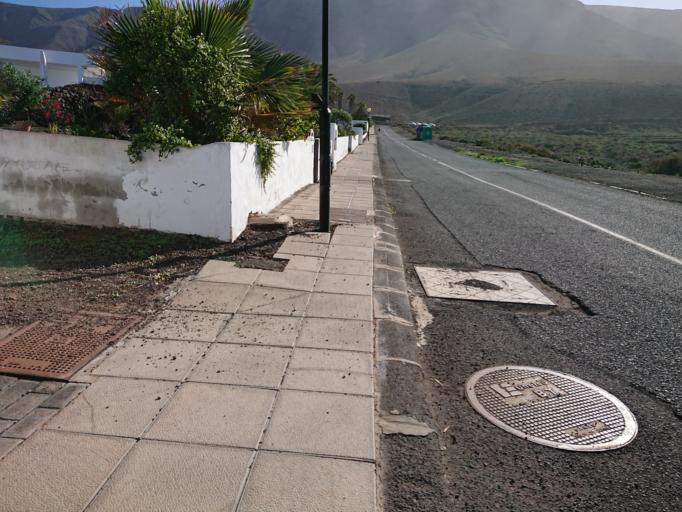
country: ES
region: Canary Islands
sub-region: Provincia de Las Palmas
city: Teguise
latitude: 29.1123
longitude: -13.5473
